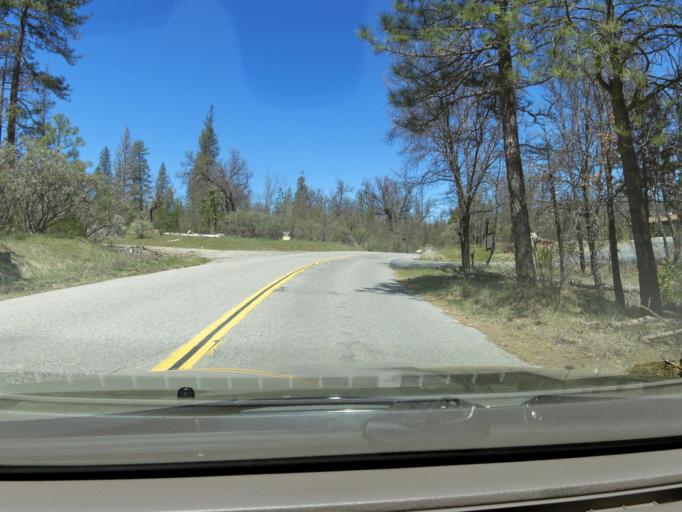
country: US
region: California
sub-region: Madera County
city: Oakhurst
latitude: 37.3291
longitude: -119.5831
